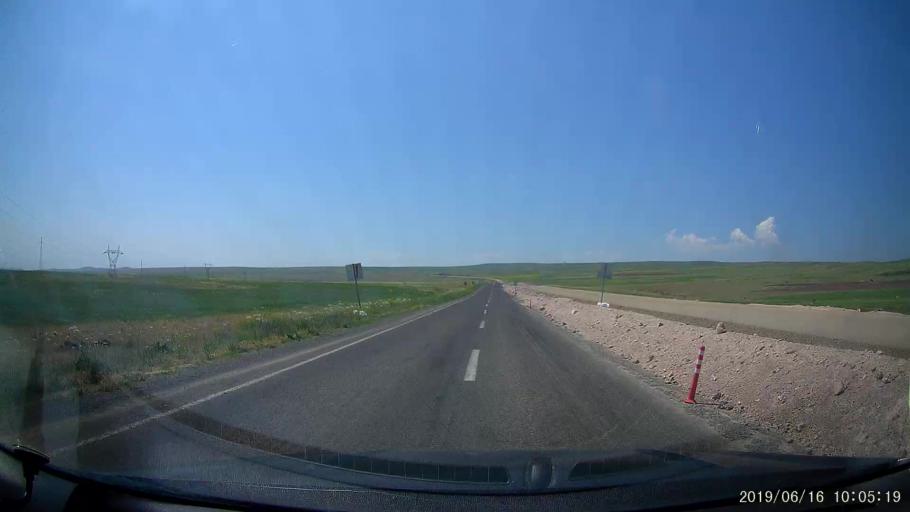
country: TR
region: Kars
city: Digor
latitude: 40.2720
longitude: 43.5381
